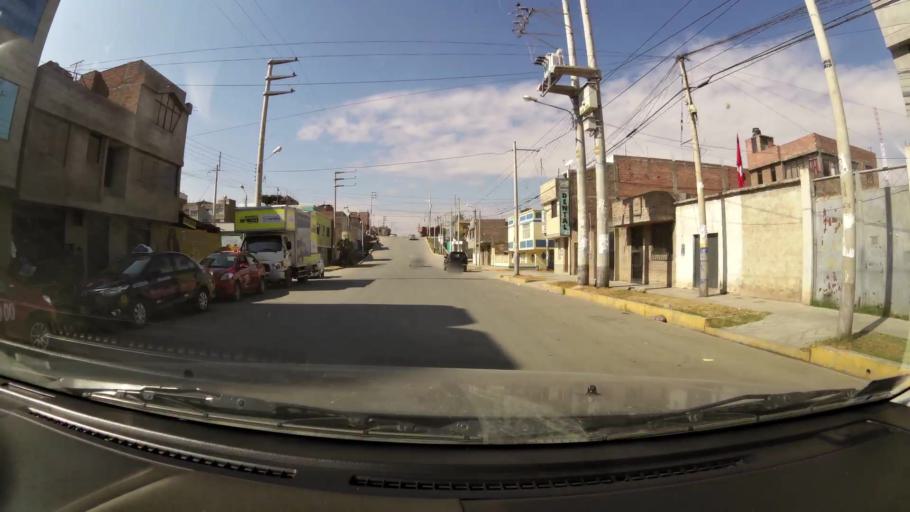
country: PE
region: Junin
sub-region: Provincia de Huancayo
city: El Tambo
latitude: -12.0756
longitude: -75.2240
